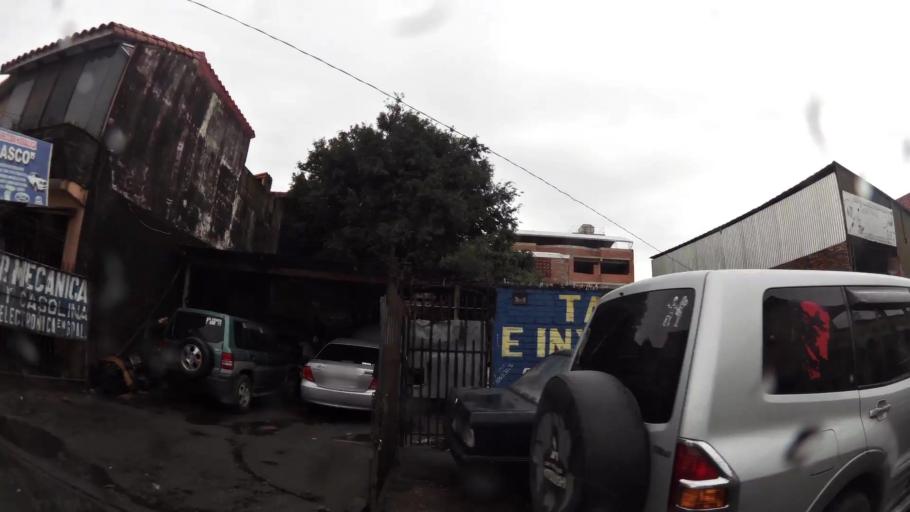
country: BO
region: Santa Cruz
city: Santa Cruz de la Sierra
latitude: -17.8104
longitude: -63.1942
